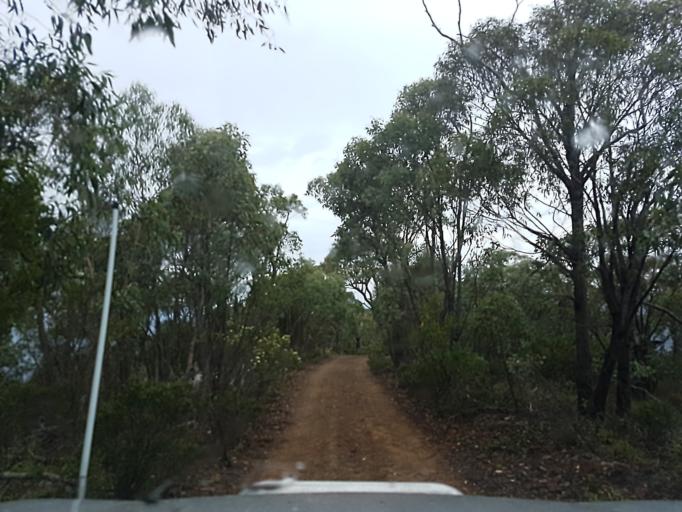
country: AU
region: New South Wales
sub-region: Snowy River
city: Jindabyne
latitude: -36.9235
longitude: 148.3477
